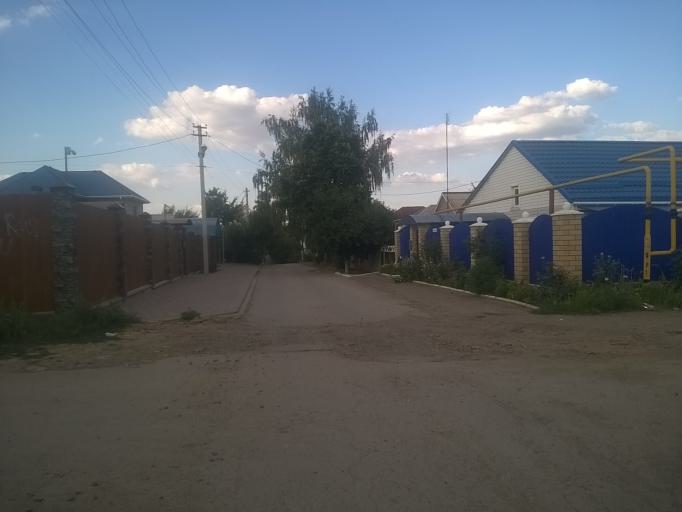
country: RU
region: Rostov
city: Donetsk
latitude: 48.3401
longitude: 39.9593
